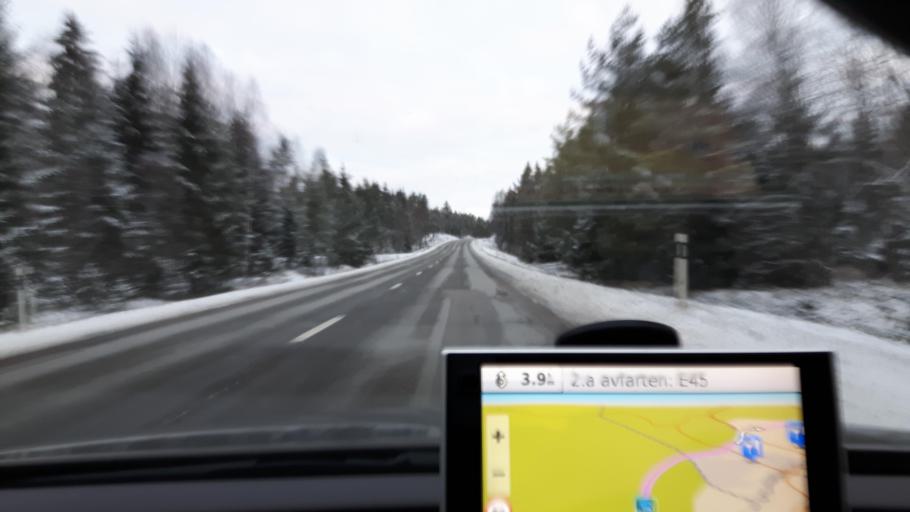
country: SE
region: Vaestra Goetaland
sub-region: Amals Kommun
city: Amal
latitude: 59.0226
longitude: 12.6820
